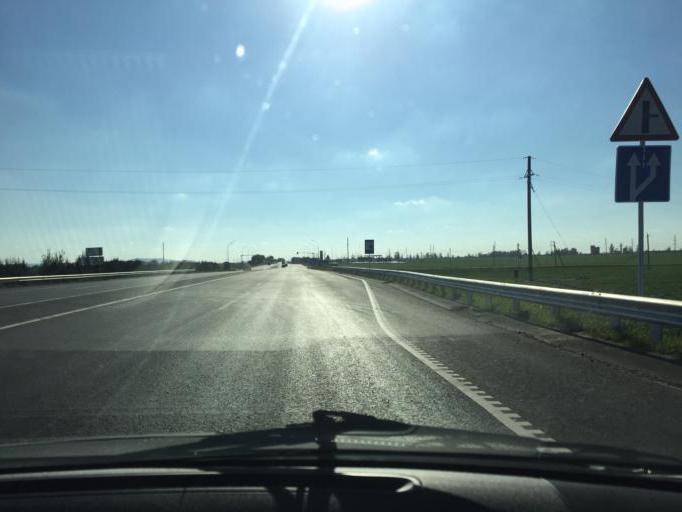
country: BY
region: Minsk
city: Slutsk
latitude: 52.9895
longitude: 27.5067
